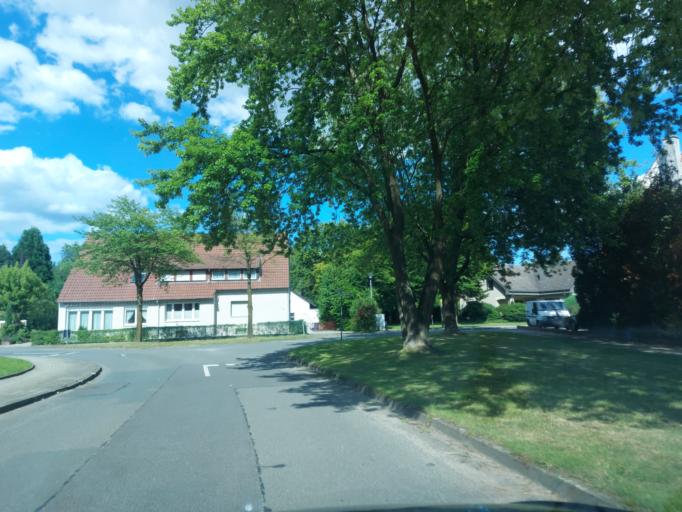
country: DE
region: Lower Saxony
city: Hagen
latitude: 52.1954
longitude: 7.9729
